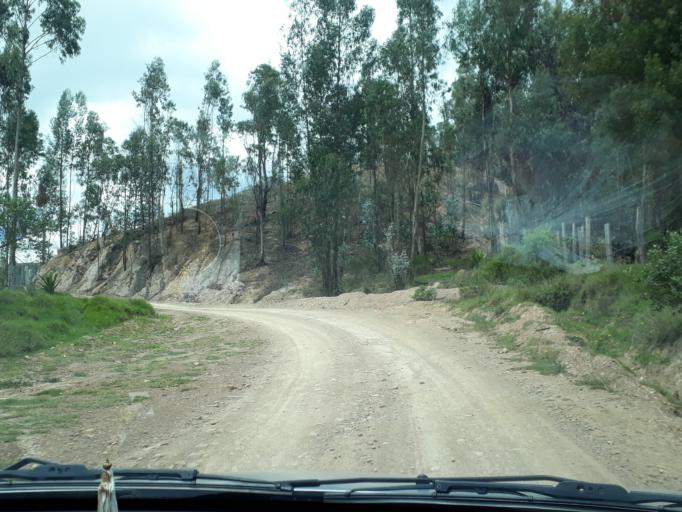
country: CO
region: Boyaca
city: Floresta
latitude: 5.8534
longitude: -72.9513
